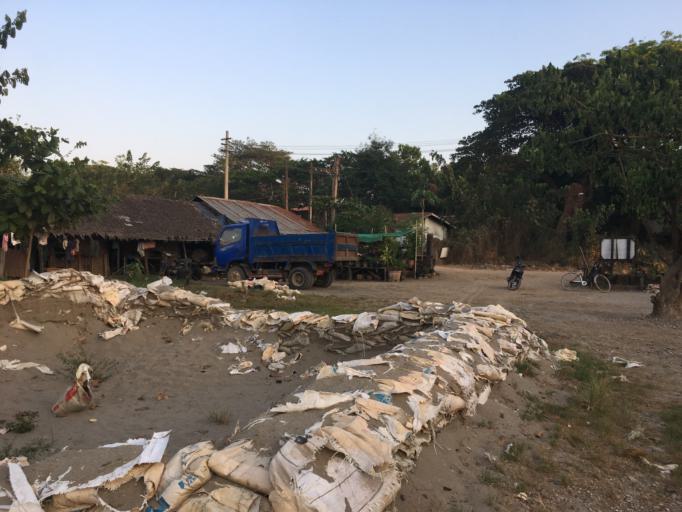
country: MM
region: Mon
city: Mawlamyine
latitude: 16.5026
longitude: 97.6229
